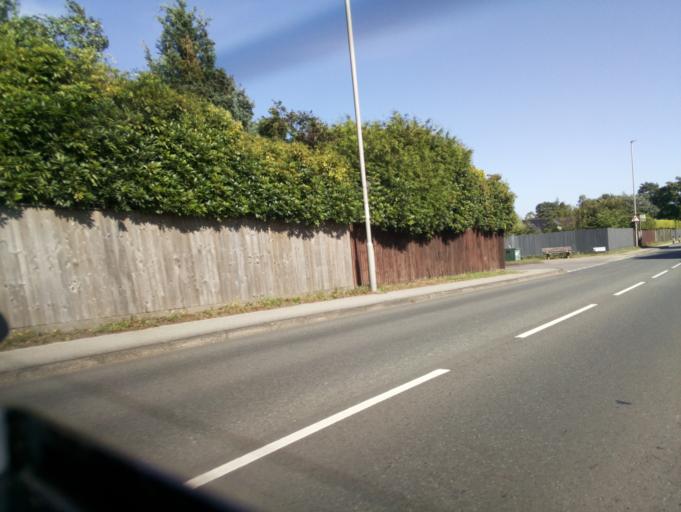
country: GB
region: England
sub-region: Dorset
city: Ferndown
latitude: 50.7880
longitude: -1.8819
